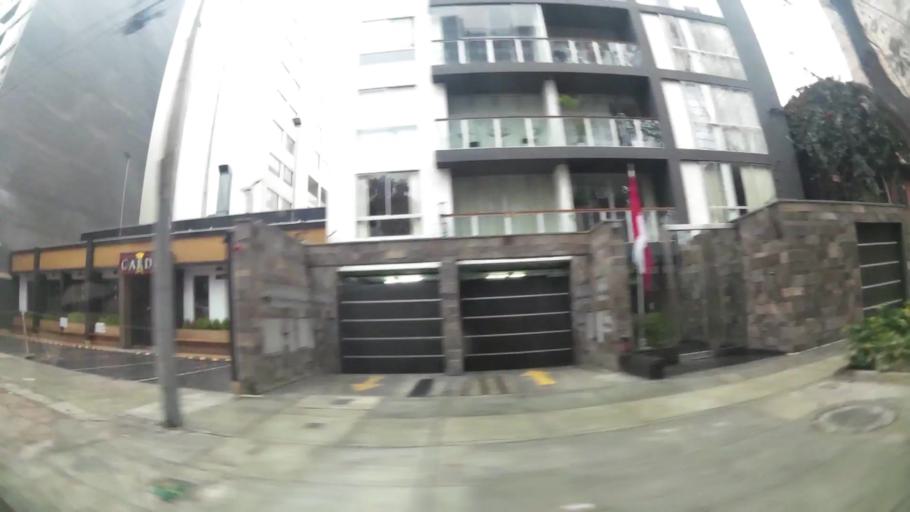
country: PE
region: Lima
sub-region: Lima
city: San Isidro
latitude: -12.1261
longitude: -77.0313
